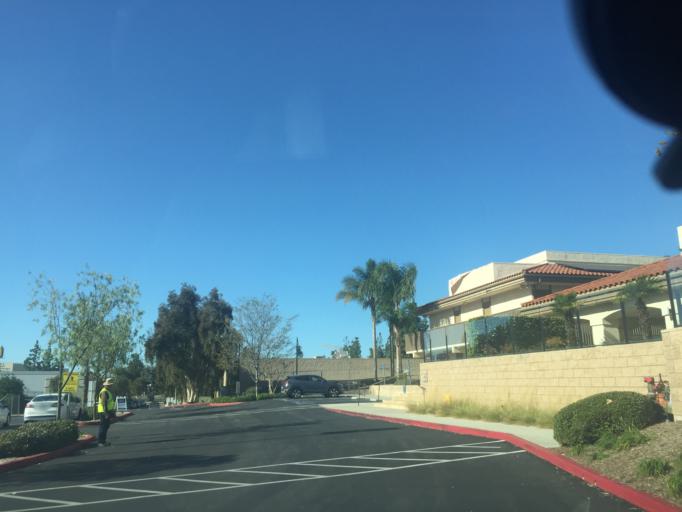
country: US
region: California
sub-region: San Diego County
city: La Mesa
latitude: 32.7818
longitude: -117.0895
